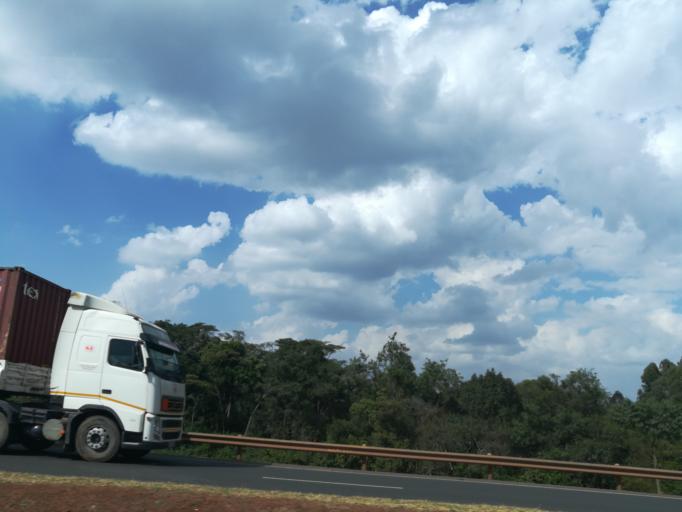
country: KE
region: Kajiado
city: Ngong
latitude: -1.3147
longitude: 36.7311
